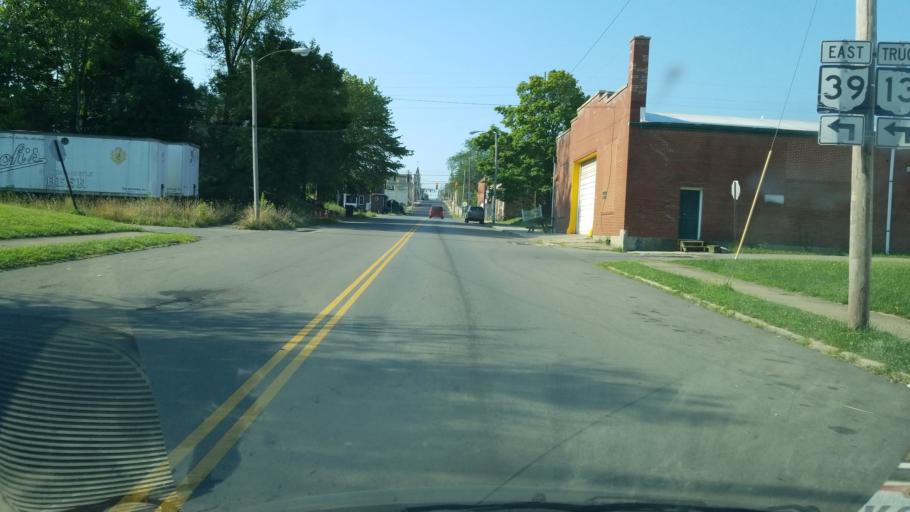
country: US
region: Ohio
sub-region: Richland County
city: Mansfield
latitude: 40.7641
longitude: -82.5176
